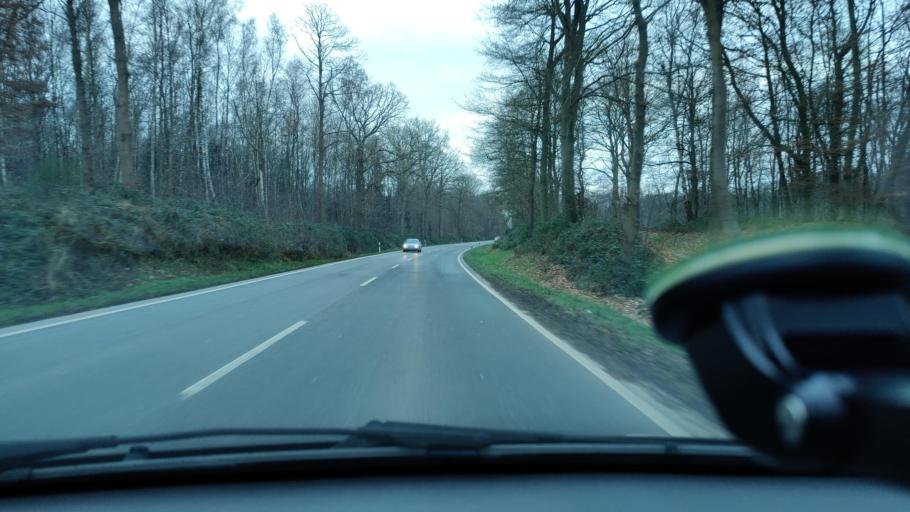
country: DE
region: North Rhine-Westphalia
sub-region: Regierungsbezirk Dusseldorf
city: Sonsbeck
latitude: 51.5933
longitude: 6.3858
